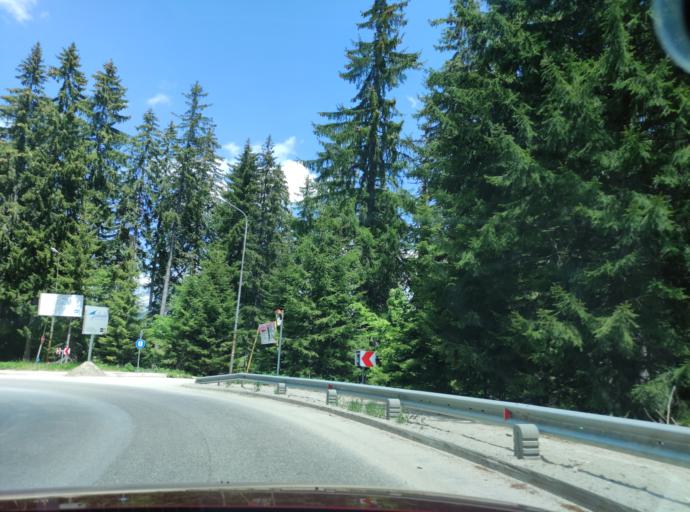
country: BG
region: Smolyan
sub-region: Obshtina Smolyan
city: Smolyan
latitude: 41.6465
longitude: 24.6989
